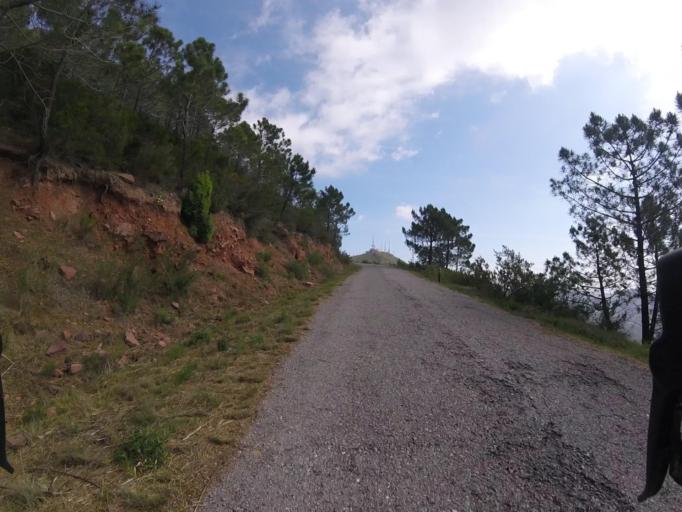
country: ES
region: Valencia
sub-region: Provincia de Castello
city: Benicassim
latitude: 40.0782
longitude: 0.0225
